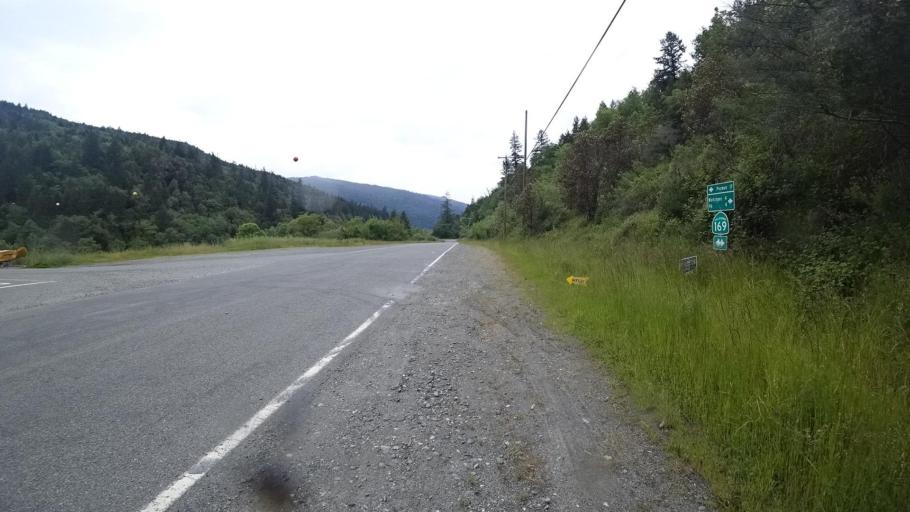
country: US
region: California
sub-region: Humboldt County
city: Willow Creek
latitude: 41.2083
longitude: -123.7554
